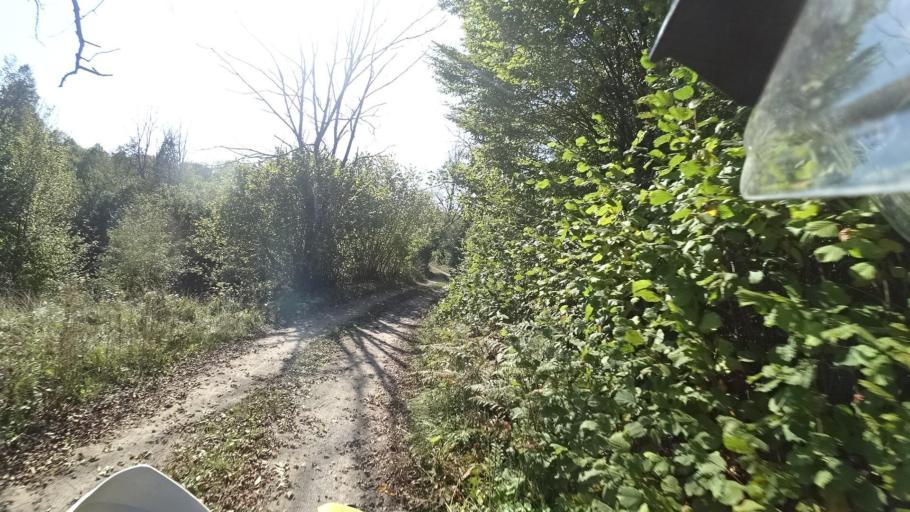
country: HR
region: Karlovacka
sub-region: Grad Ogulin
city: Ogulin
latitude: 45.1987
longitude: 15.1267
